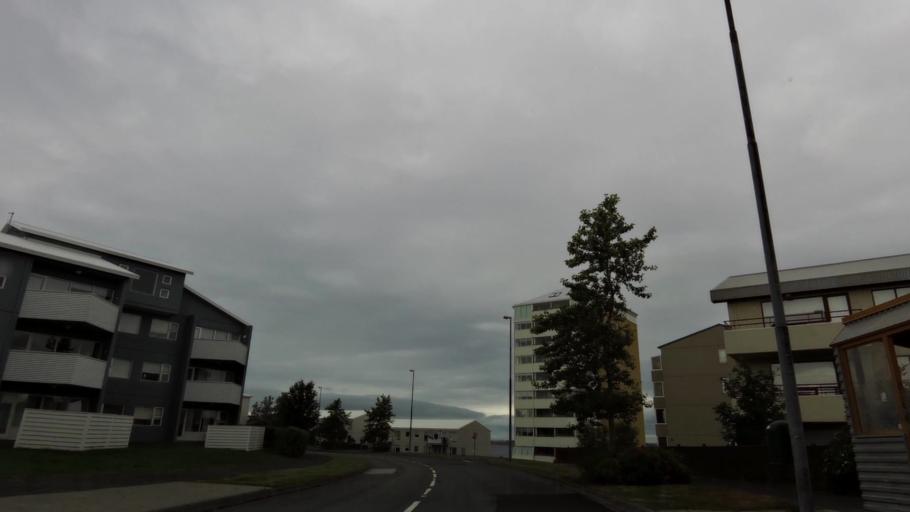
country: IS
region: Capital Region
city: Hafnarfjoerdur
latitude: 64.0570
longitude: -21.9828
